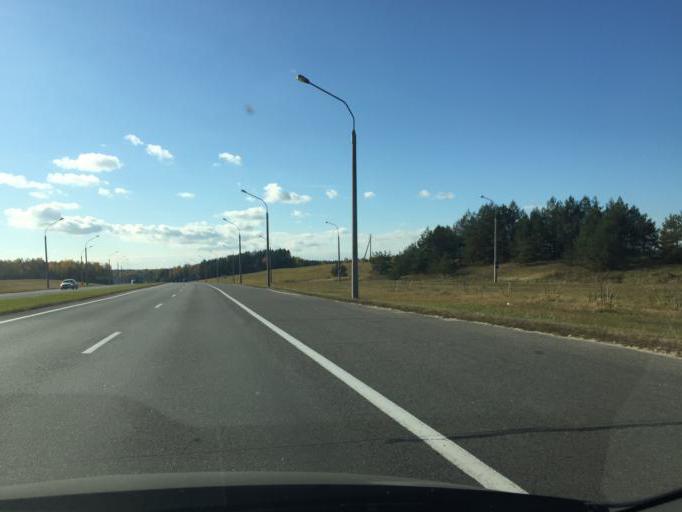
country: BY
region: Minsk
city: Slabada
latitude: 53.9477
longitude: 27.9751
